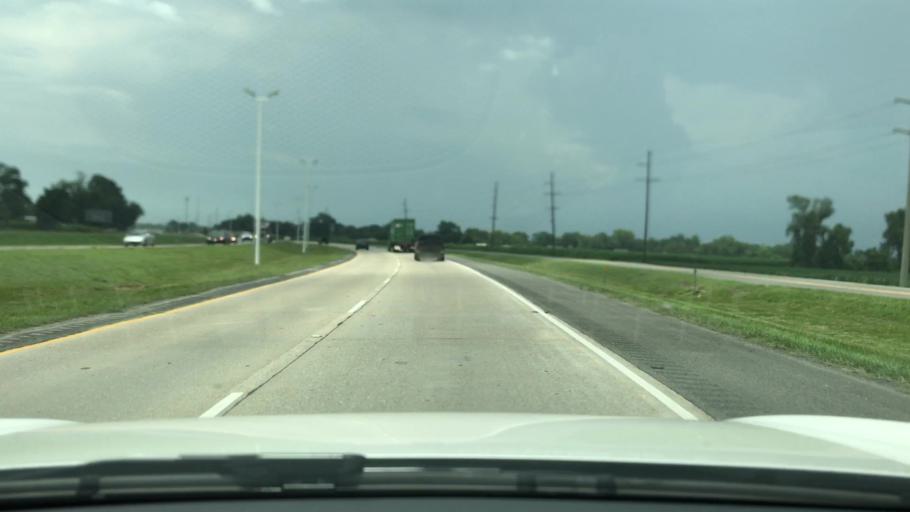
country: US
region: Louisiana
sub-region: West Baton Rouge Parish
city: Addis
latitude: 30.3490
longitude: -91.2581
